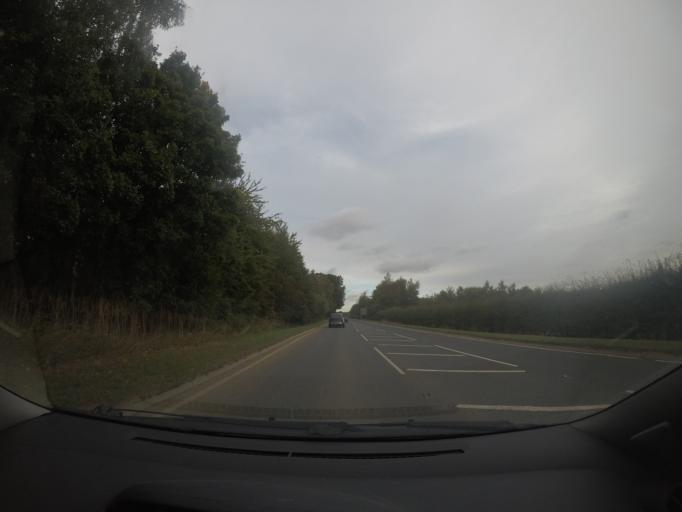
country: GB
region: England
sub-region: North Yorkshire
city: Riccall
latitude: 53.8543
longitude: -1.0495
